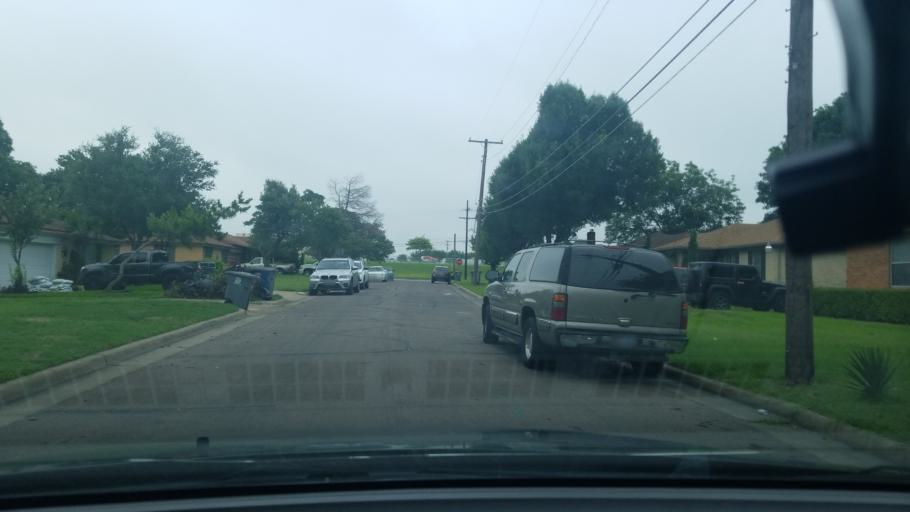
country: US
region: Texas
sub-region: Dallas County
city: Balch Springs
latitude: 32.7600
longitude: -96.6924
